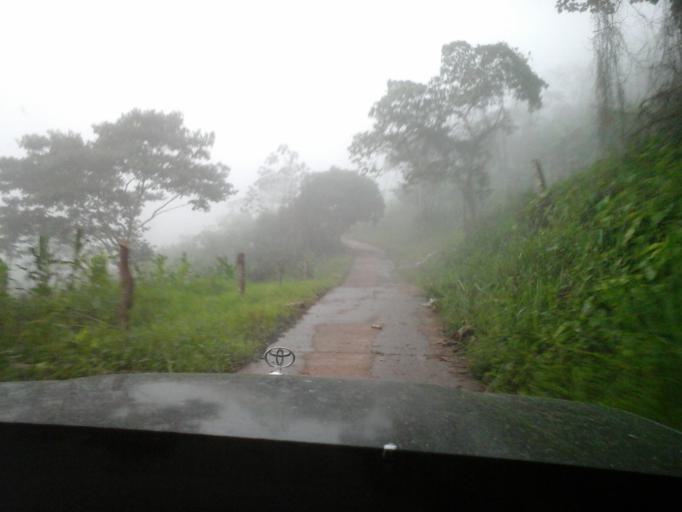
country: CO
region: Cesar
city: Agustin Codazzi
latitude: 9.9419
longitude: -73.1238
